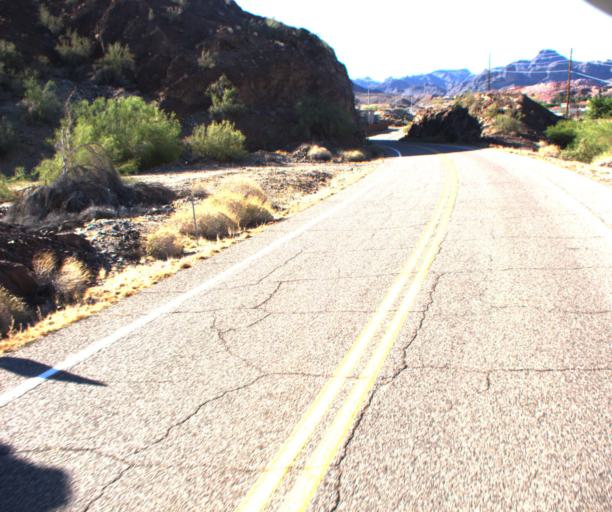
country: US
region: Arizona
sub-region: La Paz County
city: Cienega Springs
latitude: 34.2906
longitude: -114.1375
